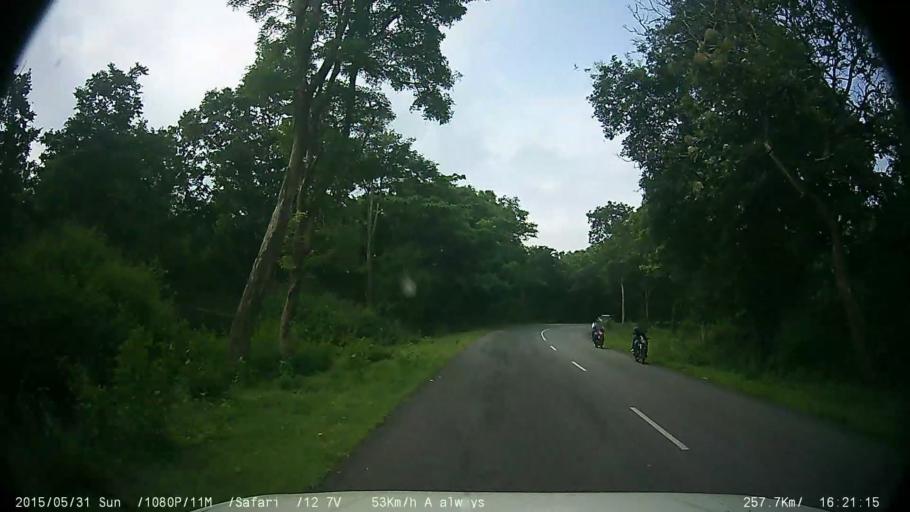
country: IN
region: Karnataka
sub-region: Chamrajnagar
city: Gundlupet
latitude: 11.7519
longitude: 76.5038
